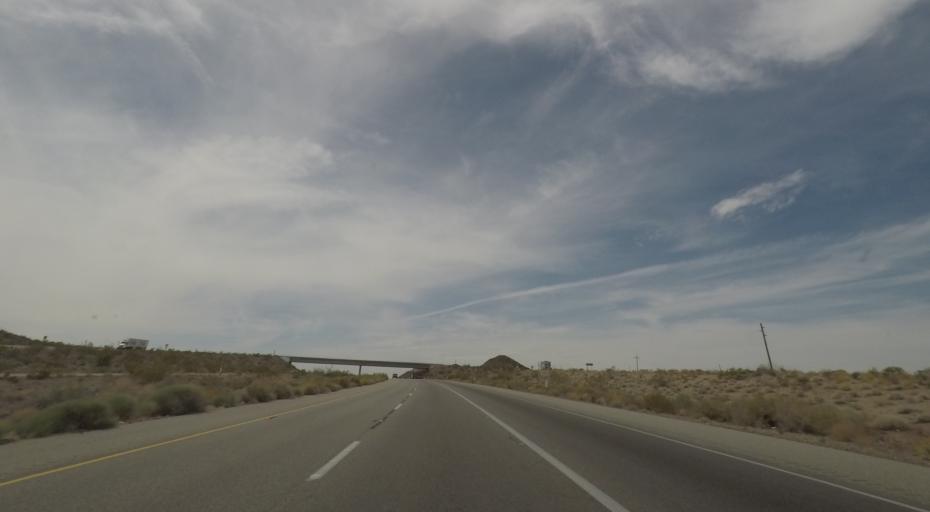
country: US
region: California
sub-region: San Bernardino County
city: Needles
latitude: 34.8307
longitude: -115.0482
